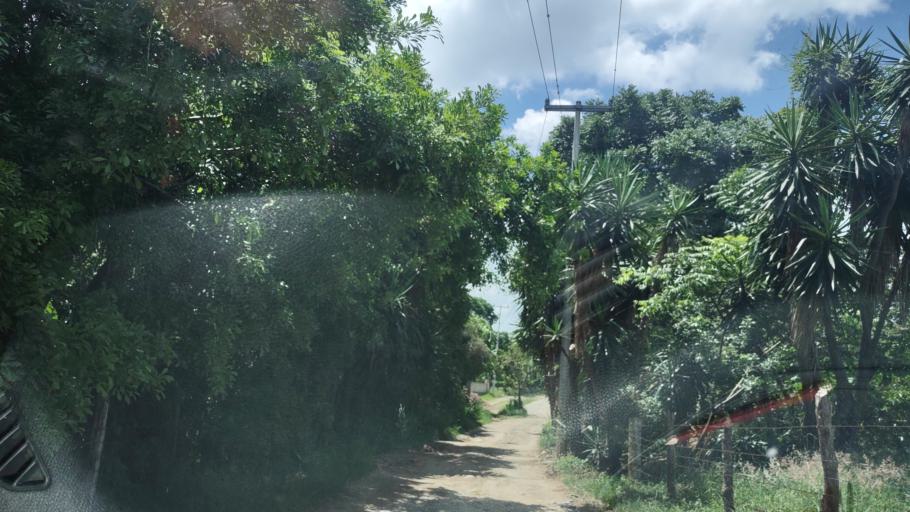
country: MX
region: Veracruz
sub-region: Emiliano Zapata
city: Dos Rios
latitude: 19.4979
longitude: -96.8124
